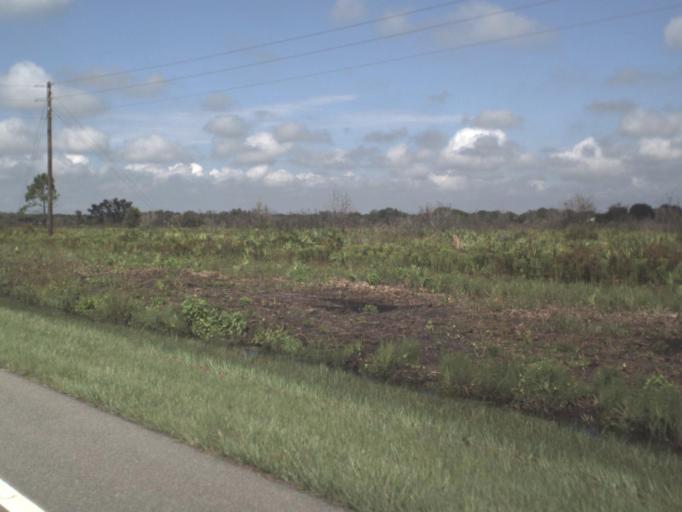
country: US
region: Florida
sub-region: Sarasota County
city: Lake Sarasota
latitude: 27.2426
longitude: -82.3286
